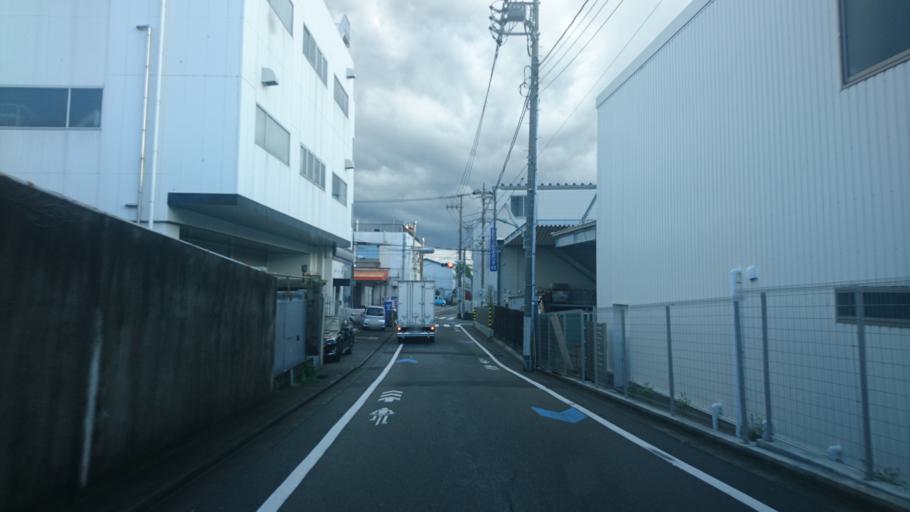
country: JP
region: Kanagawa
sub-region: Kawasaki-shi
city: Kawasaki
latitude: 35.5609
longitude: 139.7428
